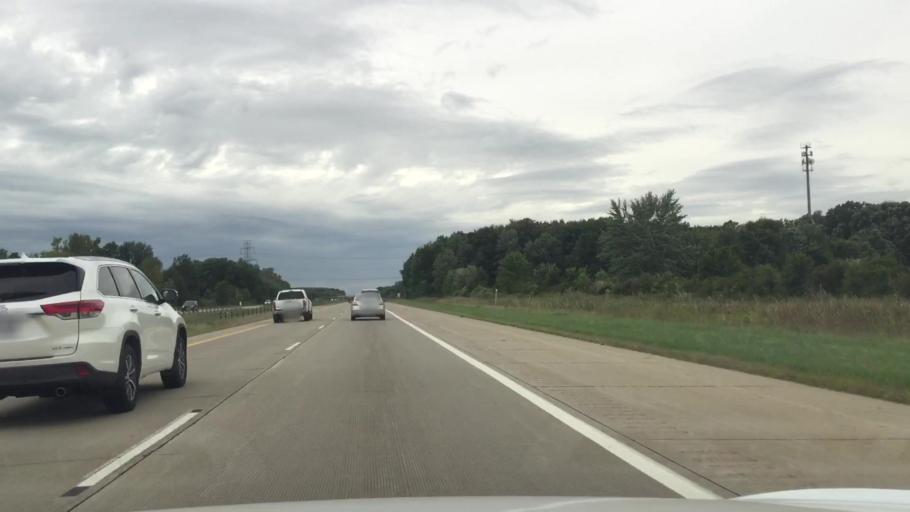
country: US
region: Michigan
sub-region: Macomb County
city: Richmond
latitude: 42.7758
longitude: -82.6795
